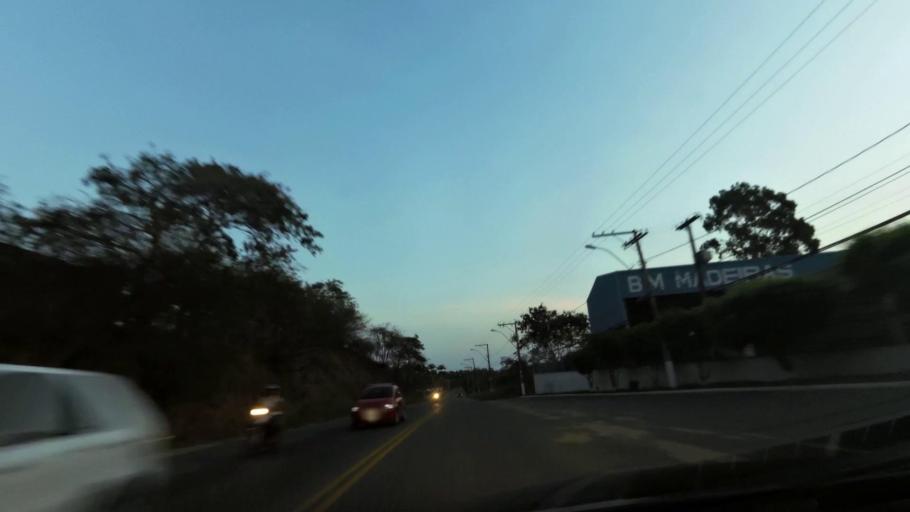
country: BR
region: Espirito Santo
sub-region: Guarapari
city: Guarapari
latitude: -20.6314
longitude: -40.4783
